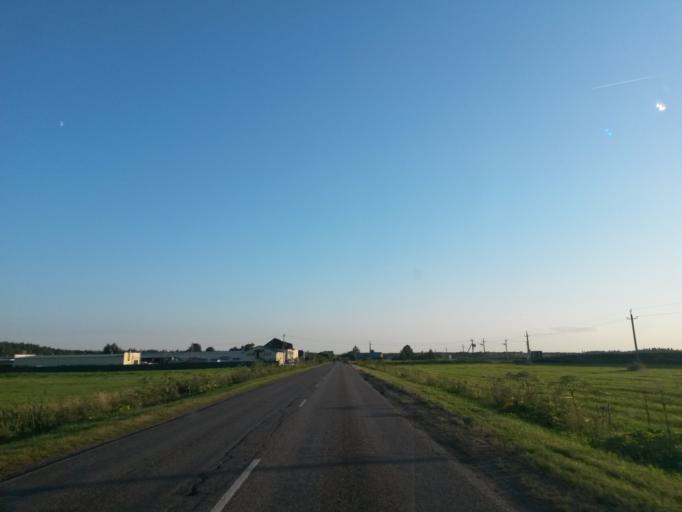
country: RU
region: Moskovskaya
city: Belyye Stolby
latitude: 55.2955
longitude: 37.7942
